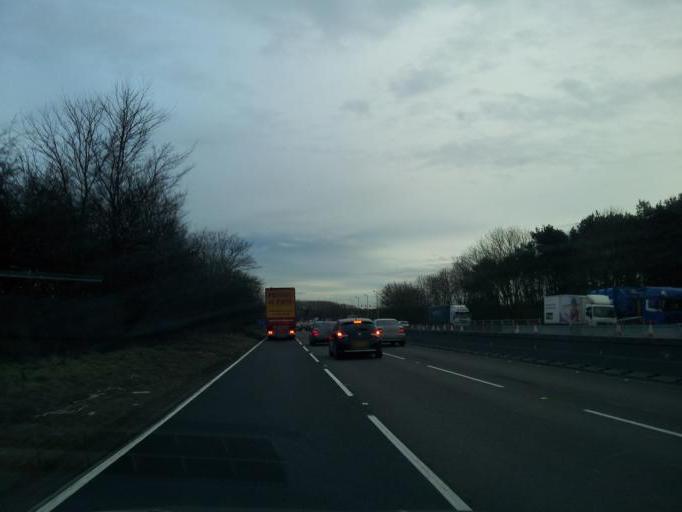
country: GB
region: England
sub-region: Northamptonshire
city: Long Buckby
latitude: 52.2824
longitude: -1.0991
